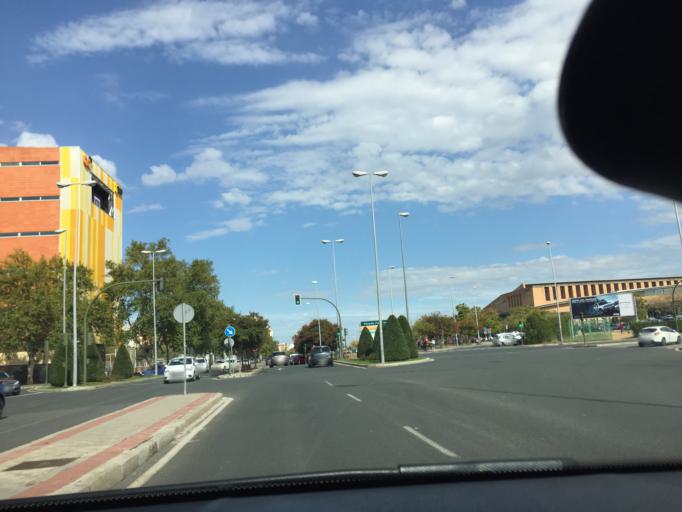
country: ES
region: Andalusia
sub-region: Provincia de Sevilla
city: Sevilla
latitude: 37.3913
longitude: -5.9787
